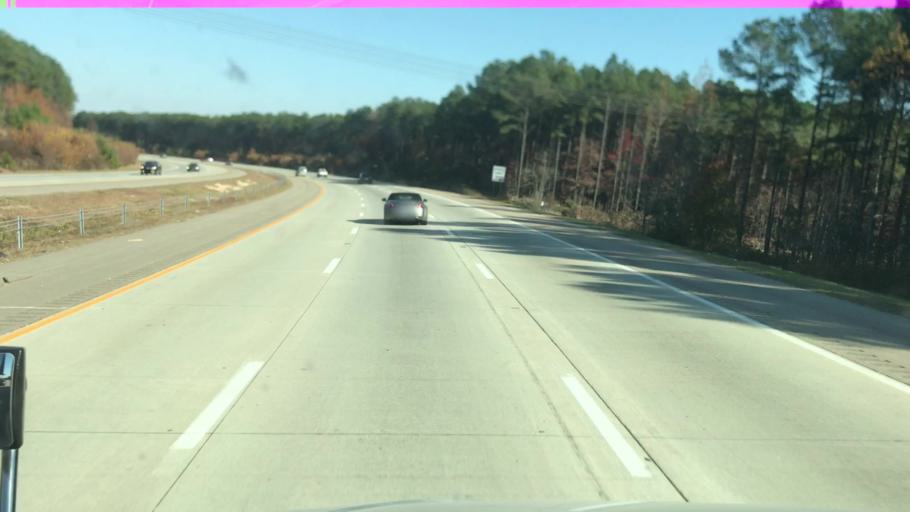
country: US
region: North Carolina
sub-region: Wake County
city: Knightdale
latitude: 35.7705
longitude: -78.4522
